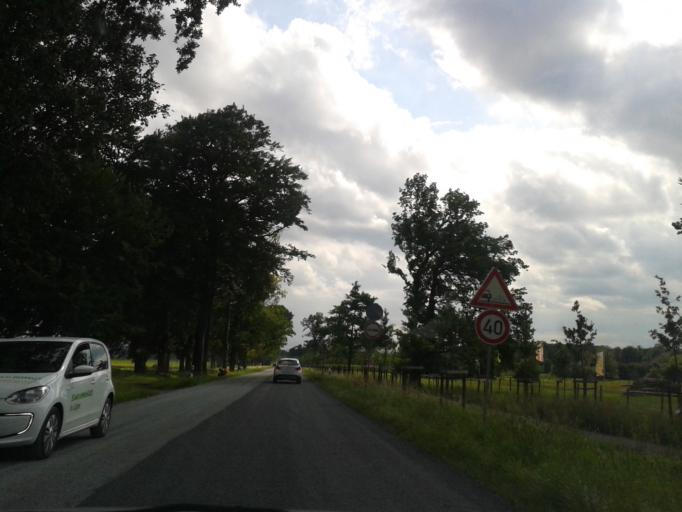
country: DE
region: North Rhine-Westphalia
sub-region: Regierungsbezirk Detmold
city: Schlangen
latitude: 51.8329
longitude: 8.8438
